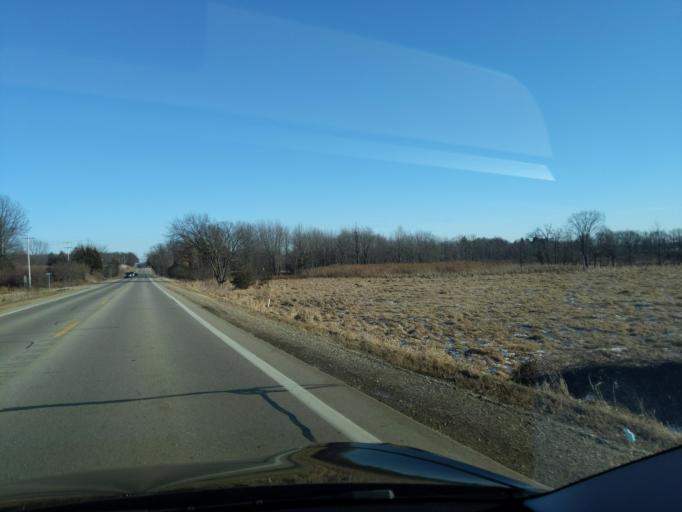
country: US
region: Michigan
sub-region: Ingham County
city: Stockbridge
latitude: 42.3946
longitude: -84.3061
